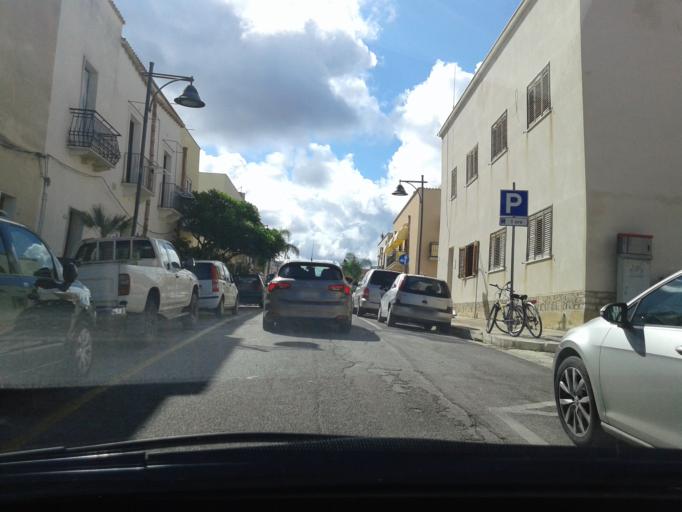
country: IT
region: Sicily
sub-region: Trapani
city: San Vito Lo Capo
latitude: 38.1731
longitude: 12.7345
